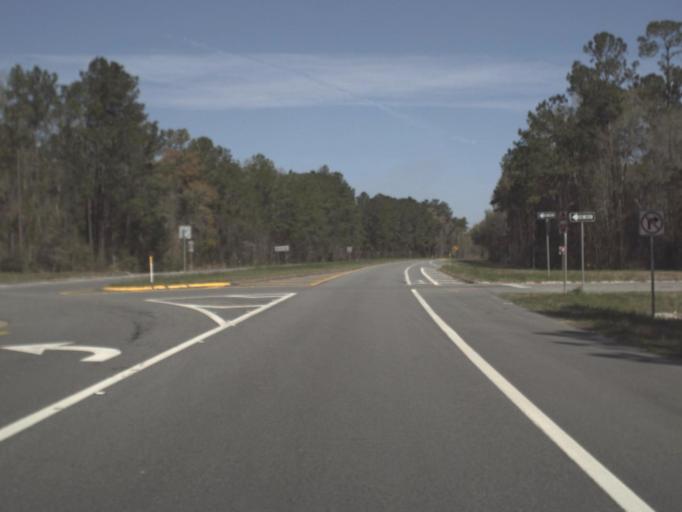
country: US
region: Florida
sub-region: Jefferson County
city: Monticello
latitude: 30.4883
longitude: -84.0255
